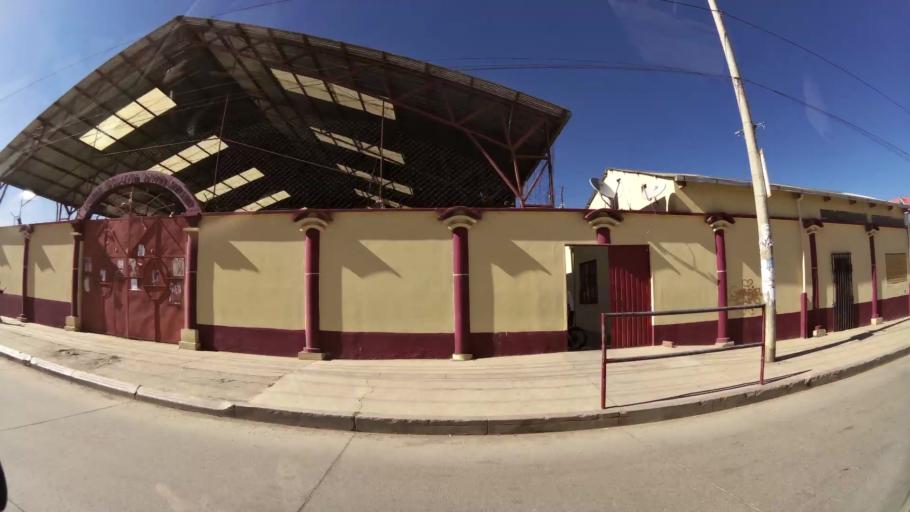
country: BO
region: La Paz
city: La Paz
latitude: -16.5346
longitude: -68.2177
